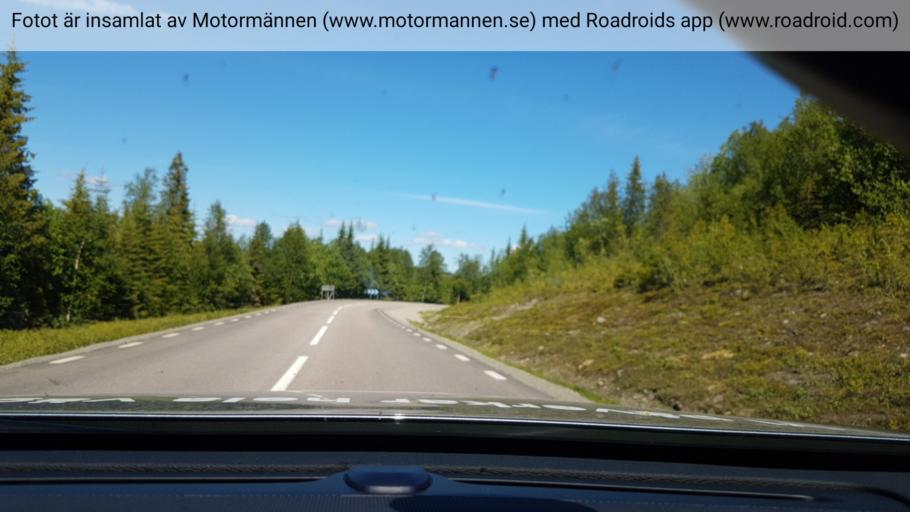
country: SE
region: Vaesterbotten
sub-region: Asele Kommun
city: Insjon
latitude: 64.7300
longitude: 17.5181
